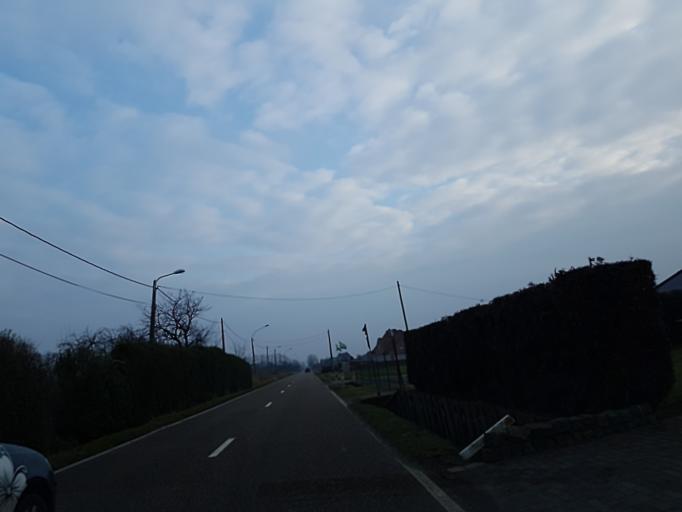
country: BE
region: Flanders
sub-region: Provincie Antwerpen
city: Stabroek
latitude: 51.3166
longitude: 4.3820
